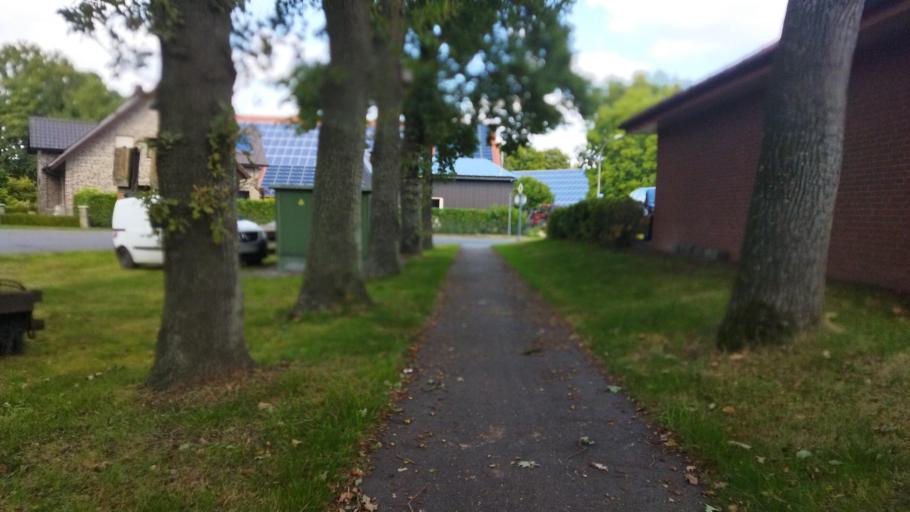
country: DE
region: Lower Saxony
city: Haren
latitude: 52.8126
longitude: 7.2568
